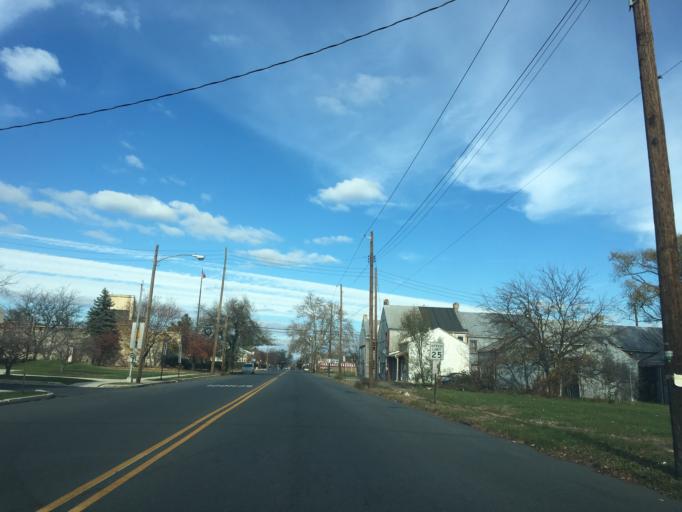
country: US
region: Pennsylvania
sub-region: Dauphin County
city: Harrisburg
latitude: 40.2771
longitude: -76.8886
